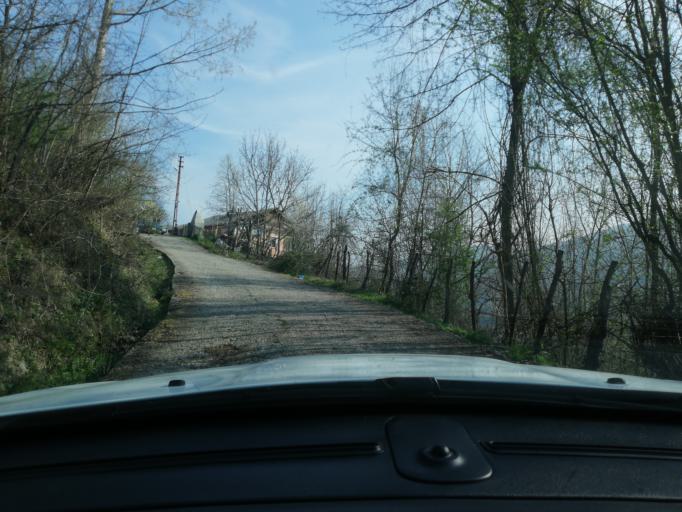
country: TR
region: Karabuk
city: Yenice
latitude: 41.2684
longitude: 32.3601
